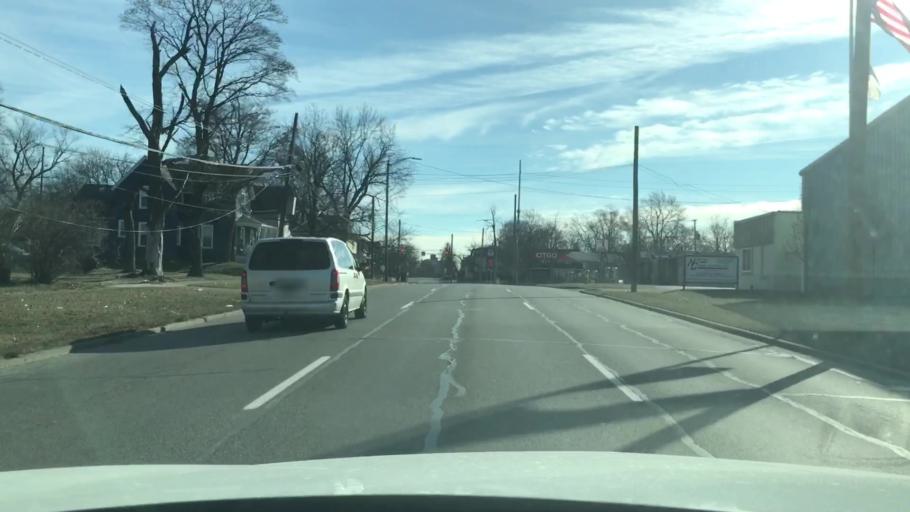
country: US
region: Michigan
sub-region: Oakland County
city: Pontiac
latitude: 42.6456
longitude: -83.3054
